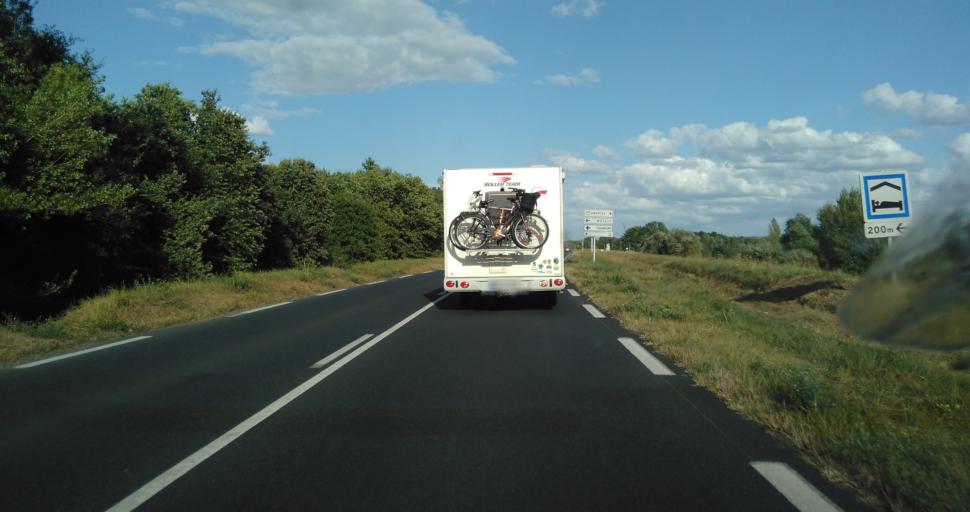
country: FR
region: Centre
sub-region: Departement d'Indre-et-Loire
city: Noizay
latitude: 47.4045
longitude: 0.8955
